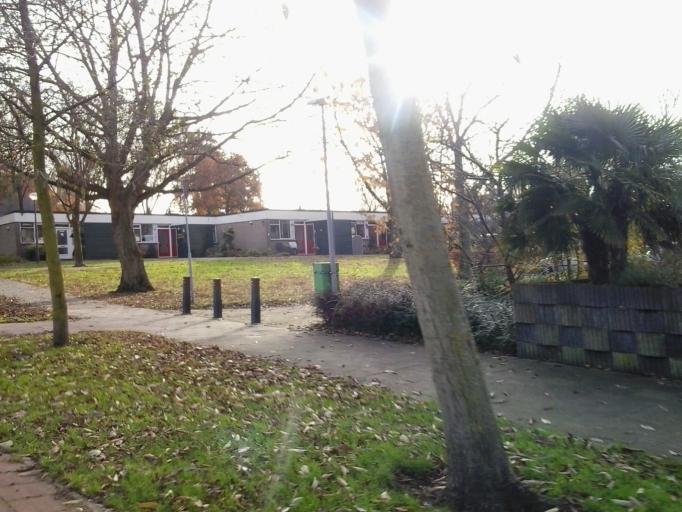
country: NL
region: South Holland
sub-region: Gemeente Lansingerland
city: Bergschenhoek
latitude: 51.9906
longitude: 4.4981
